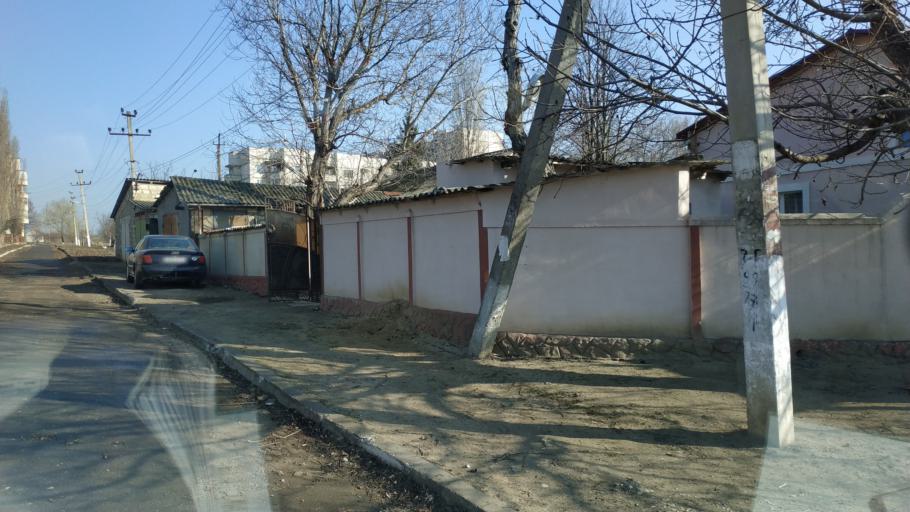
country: MD
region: Chisinau
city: Singera
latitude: 46.6849
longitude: 29.0553
